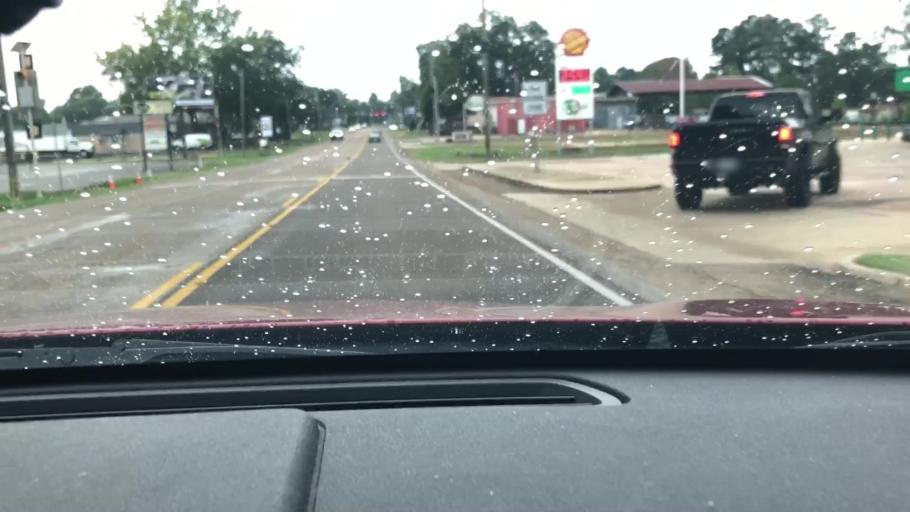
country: US
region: Texas
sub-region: Bowie County
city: Nash
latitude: 33.4425
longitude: -94.1271
